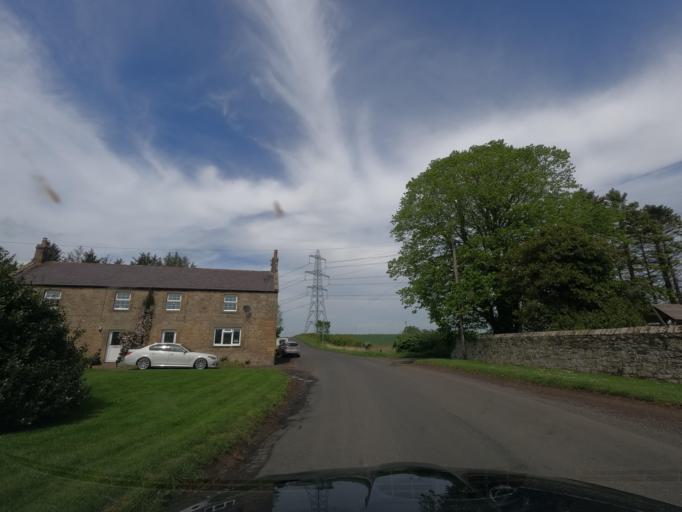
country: GB
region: England
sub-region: Northumberland
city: Whittingham
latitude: 55.4079
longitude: -1.8905
